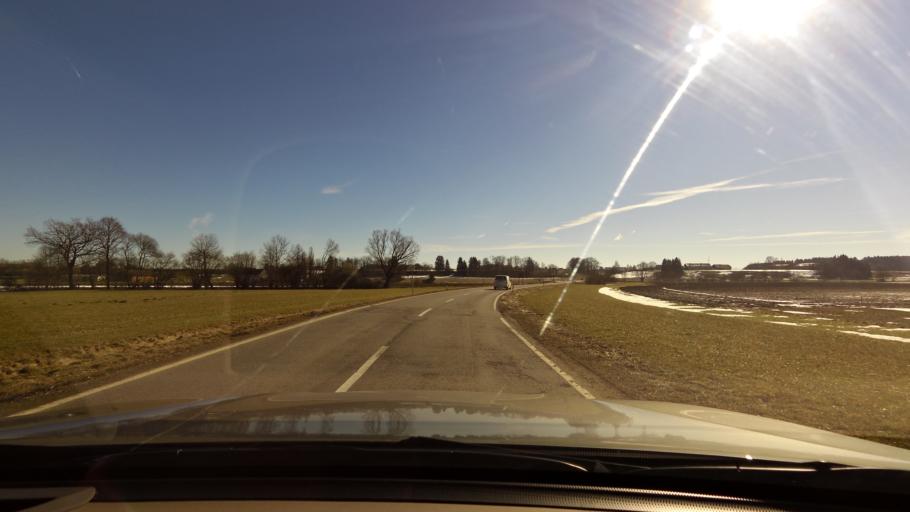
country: DE
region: Bavaria
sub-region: Upper Bavaria
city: Taufkirchen
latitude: 48.1430
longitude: 12.4511
